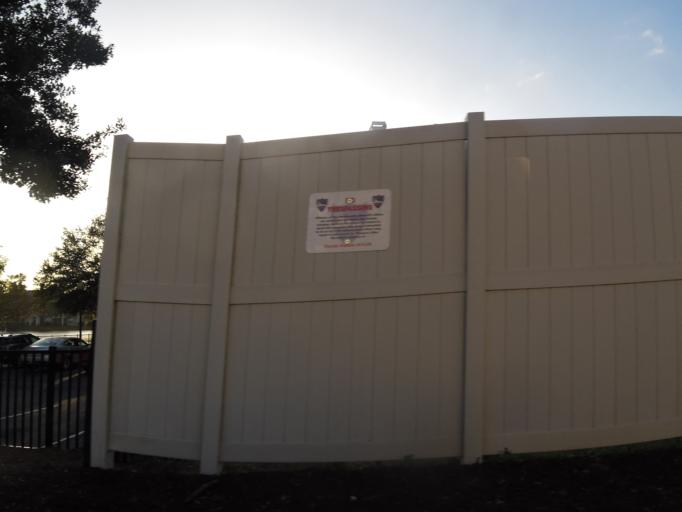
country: US
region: Florida
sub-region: Duval County
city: Jacksonville
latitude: 30.2679
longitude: -81.5615
